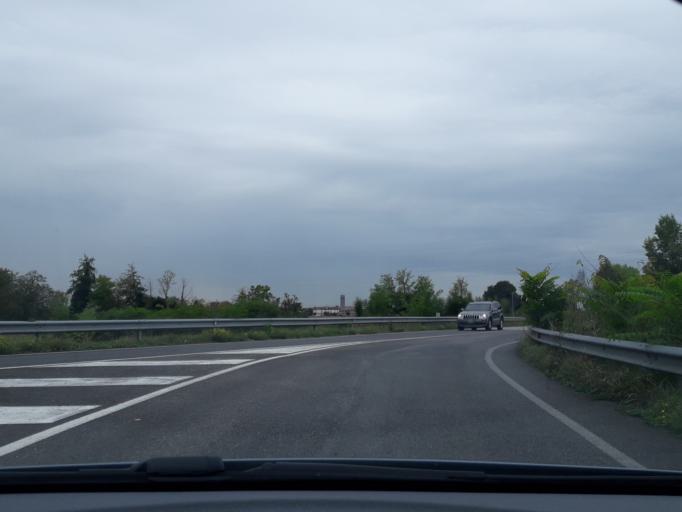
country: IT
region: Friuli Venezia Giulia
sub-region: Provincia di Udine
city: Povoletto
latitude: 46.1105
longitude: 13.2706
